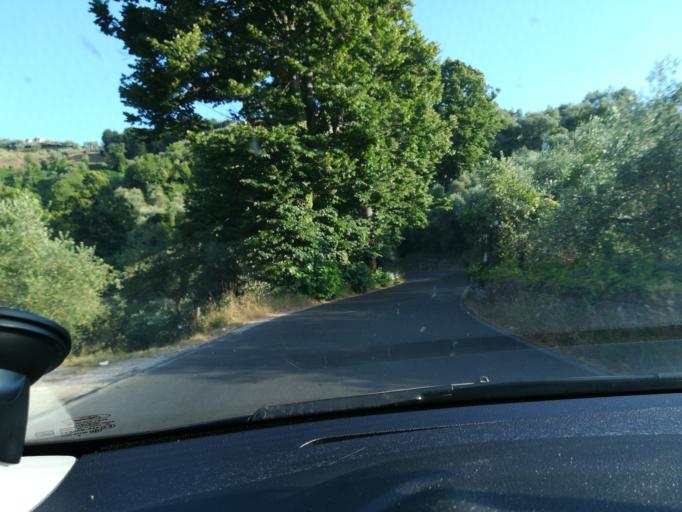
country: IT
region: Tuscany
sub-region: Provincia di Lucca
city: Stiava
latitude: 43.9147
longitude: 10.3402
